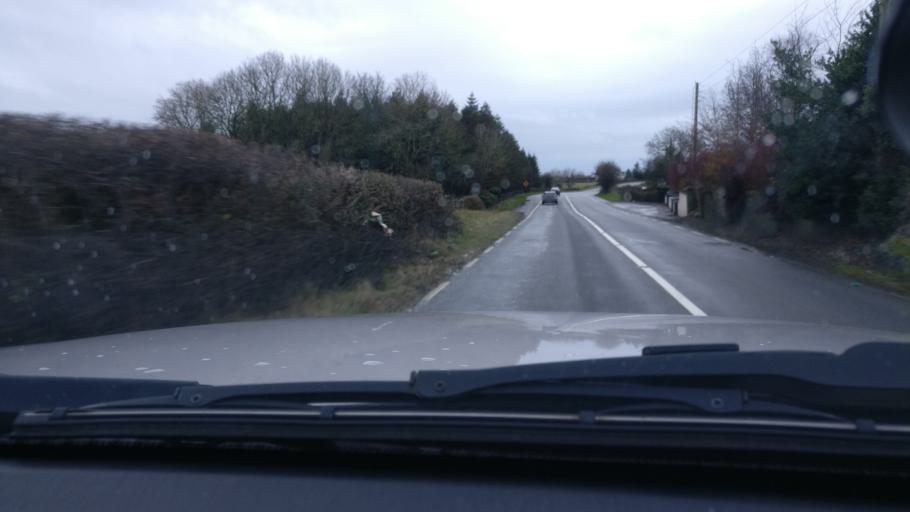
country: IE
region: Leinster
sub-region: An Longfort
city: Ballymahon
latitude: 53.5124
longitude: -7.8245
